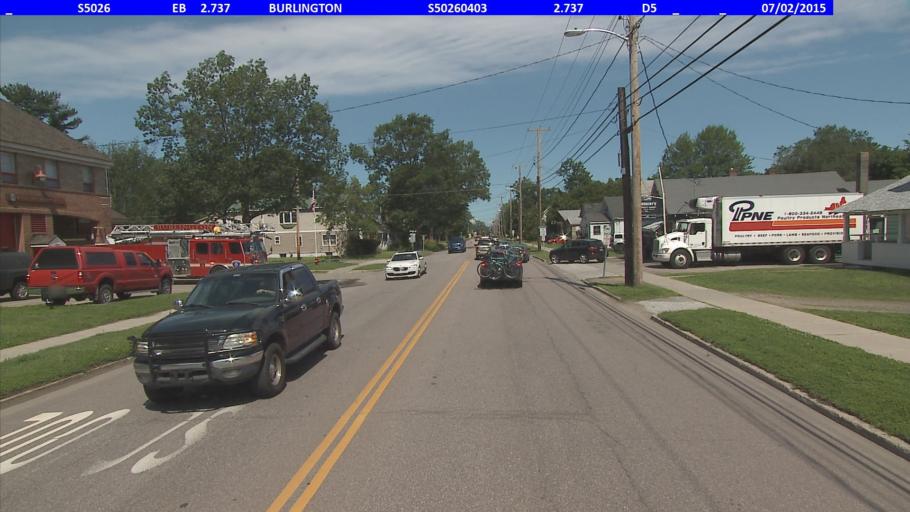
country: US
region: Vermont
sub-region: Chittenden County
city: Burlington
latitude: 44.5121
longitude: -73.2518
